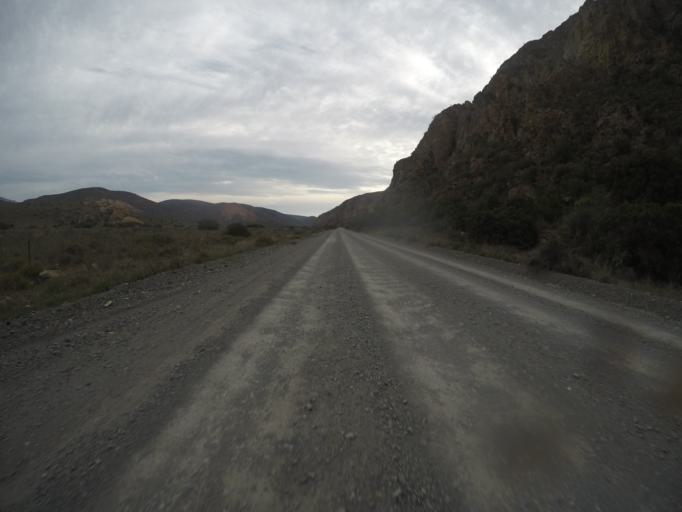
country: ZA
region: Eastern Cape
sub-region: Cacadu District Municipality
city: Willowmore
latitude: -33.5198
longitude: 23.6693
